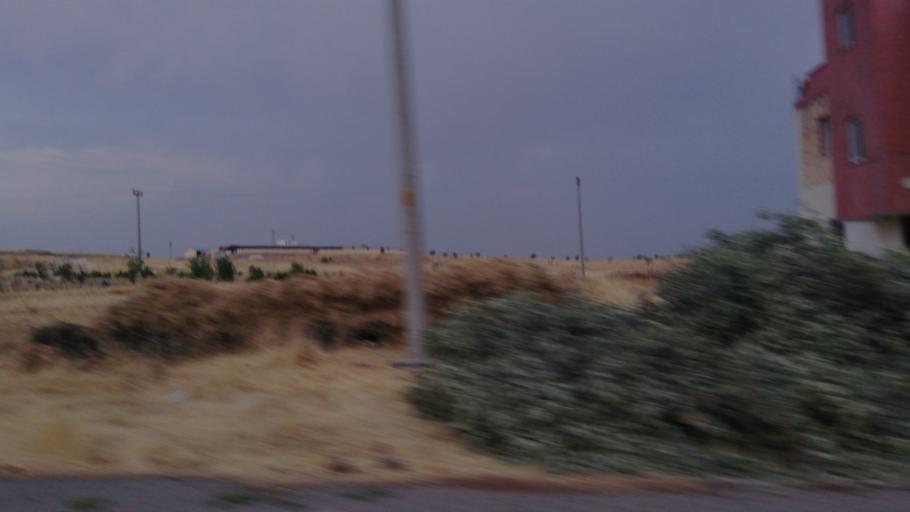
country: TR
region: Mardin
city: Kindirip
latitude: 37.4598
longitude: 41.2249
